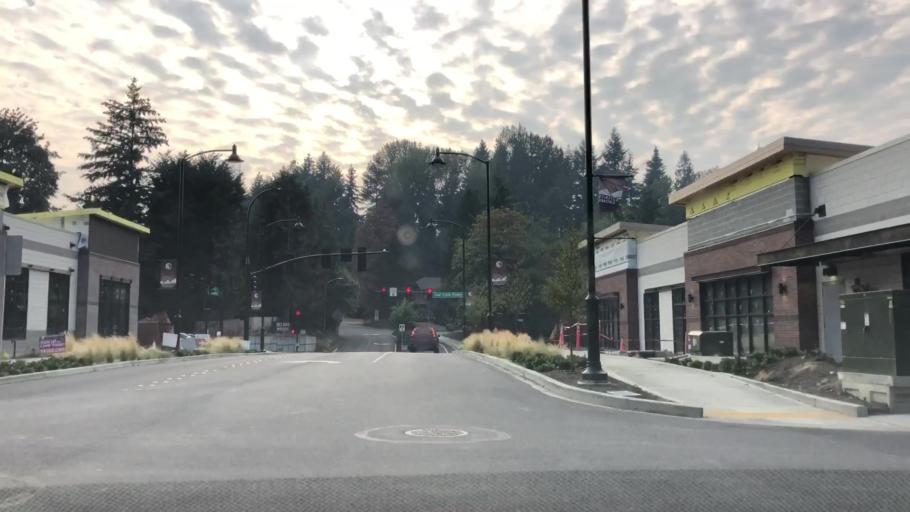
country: US
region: Washington
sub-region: King County
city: Newcastle
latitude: 47.5437
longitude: -122.1630
